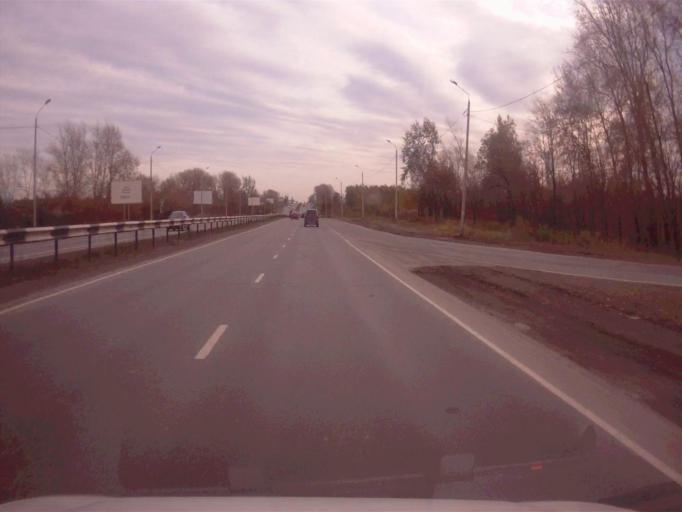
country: RU
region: Chelyabinsk
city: Novosineglazovskiy
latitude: 55.0605
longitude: 61.4018
